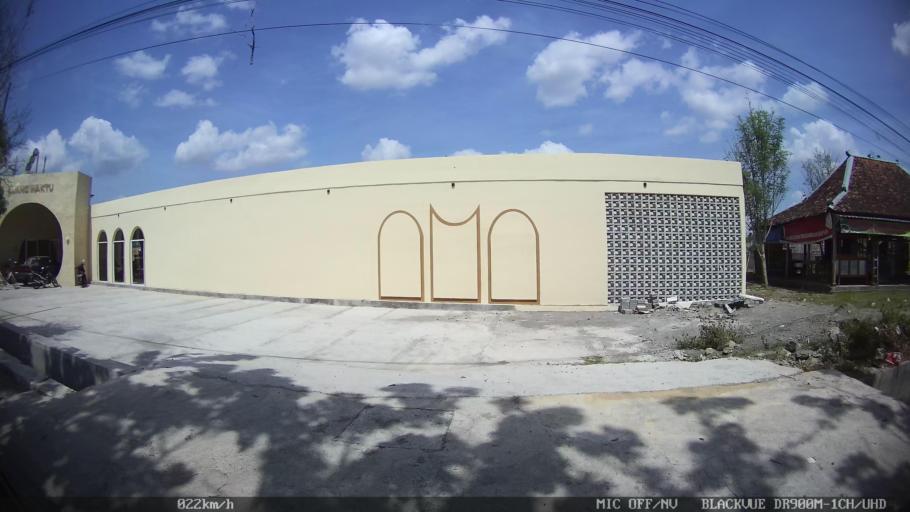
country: ID
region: Daerah Istimewa Yogyakarta
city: Sewon
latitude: -7.8316
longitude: 110.3858
